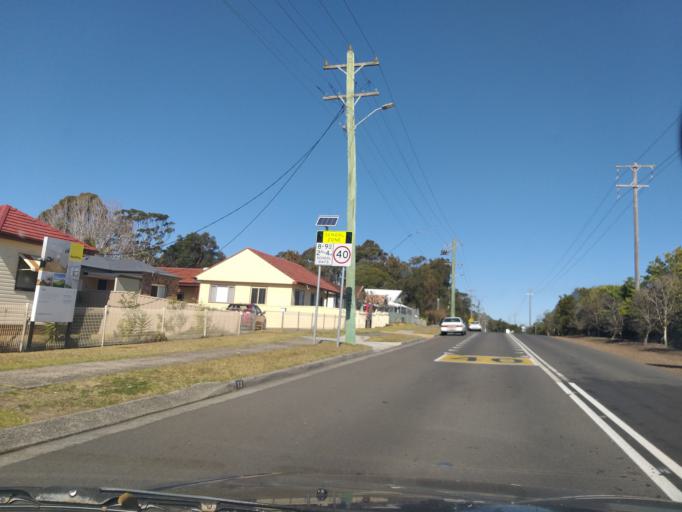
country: AU
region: New South Wales
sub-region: Wollongong
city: Bulli
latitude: -34.3504
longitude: 150.9152
